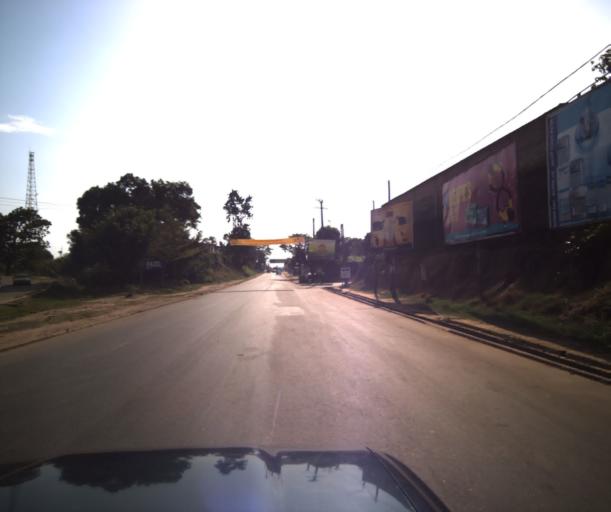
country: CM
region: Littoral
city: Bonaberi
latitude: 4.0711
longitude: 9.6895
